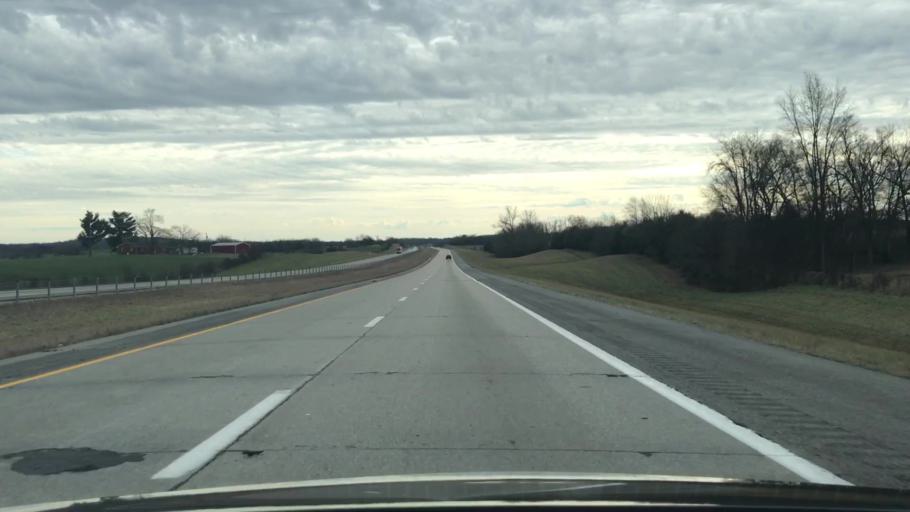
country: US
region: Kentucky
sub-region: Trigg County
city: Cadiz
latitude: 36.9223
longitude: -87.8015
